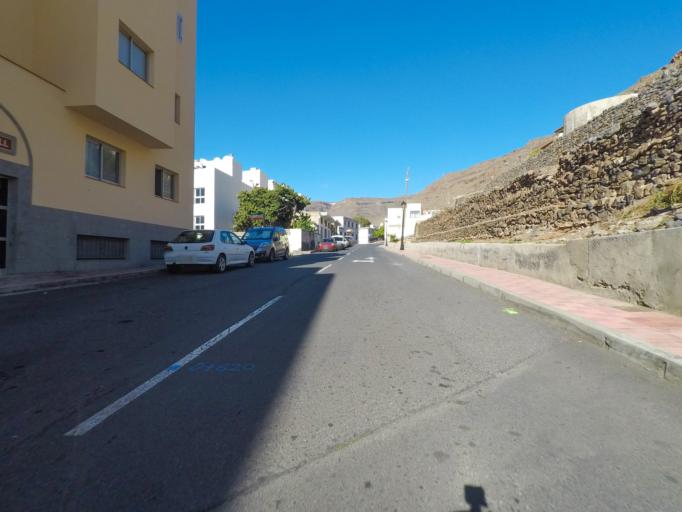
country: ES
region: Canary Islands
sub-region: Provincia de Santa Cruz de Tenerife
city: Alajero
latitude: 28.0311
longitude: -17.1984
